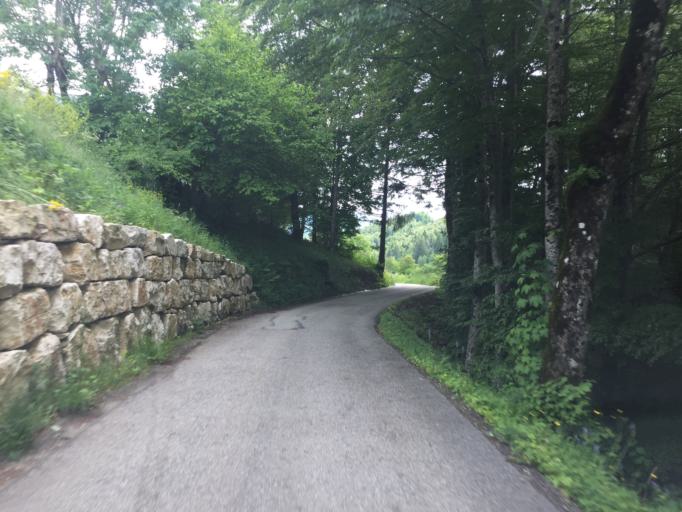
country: FR
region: Rhone-Alpes
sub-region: Departement de la Savoie
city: Vimines
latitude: 45.4736
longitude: 5.8933
